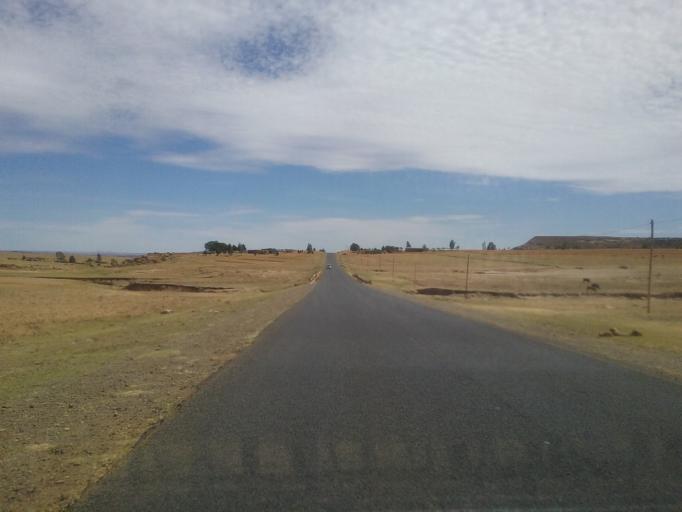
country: LS
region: Mafeteng
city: Mafeteng
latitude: -29.8873
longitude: 27.2502
